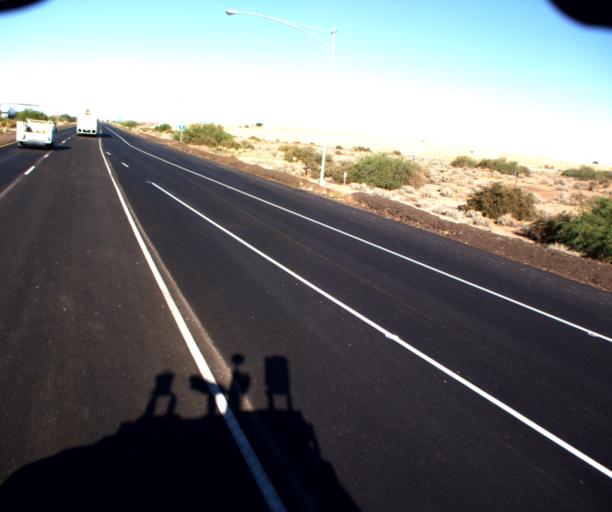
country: US
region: Arizona
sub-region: Pinal County
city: Casa Grande
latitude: 32.8282
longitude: -111.7442
